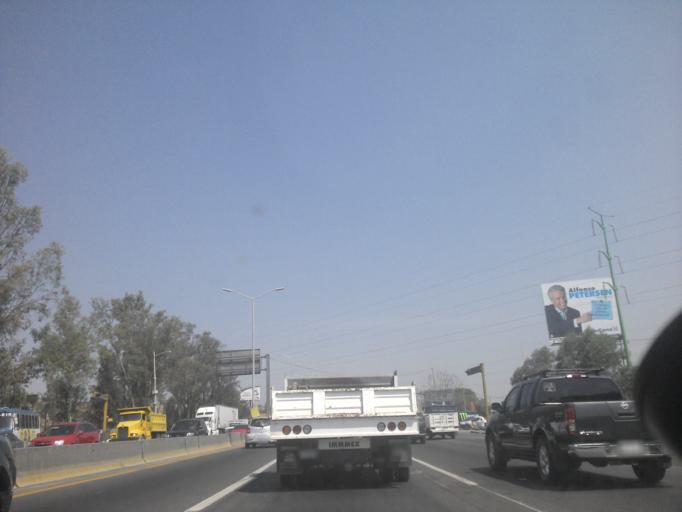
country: MX
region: Jalisco
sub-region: San Pedro Tlaquepaque
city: Paseo del Prado
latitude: 20.5913
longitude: -103.3863
